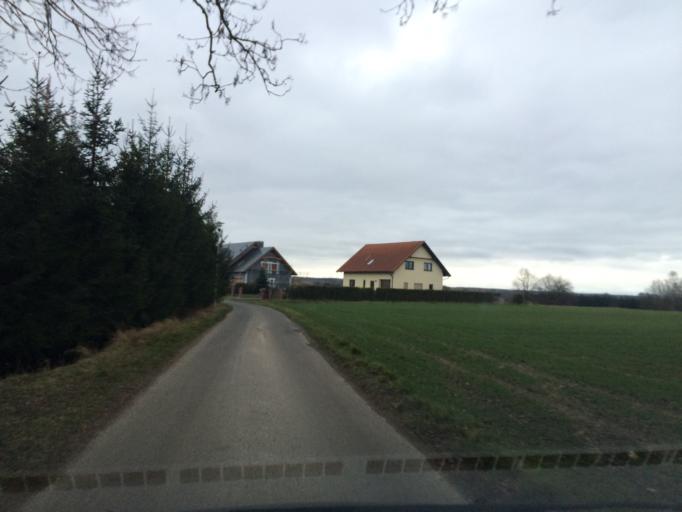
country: PL
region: Lower Silesian Voivodeship
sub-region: Powiat lubanski
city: Luban
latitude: 51.1480
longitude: 15.3064
